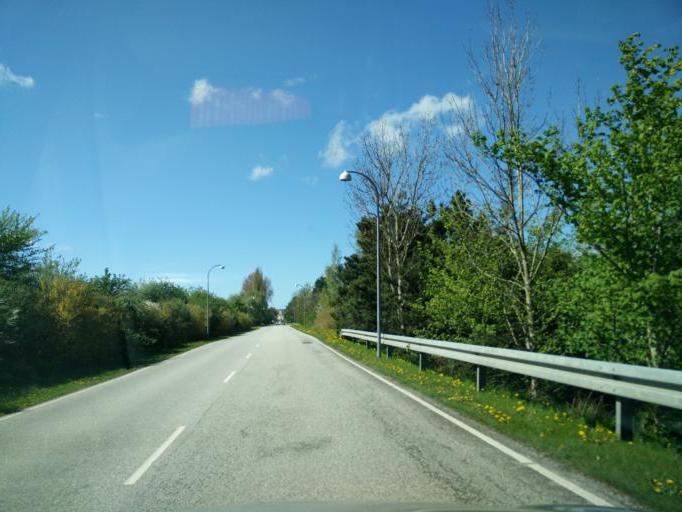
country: DK
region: Capital Region
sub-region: Gribskov Kommune
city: Helsinge
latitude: 56.0114
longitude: 12.2144
